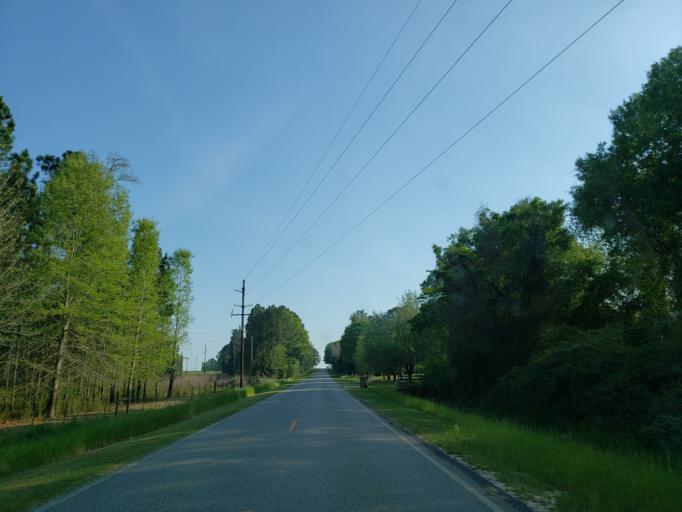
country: US
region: Georgia
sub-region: Tift County
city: Tifton
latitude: 31.5233
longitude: -83.5598
